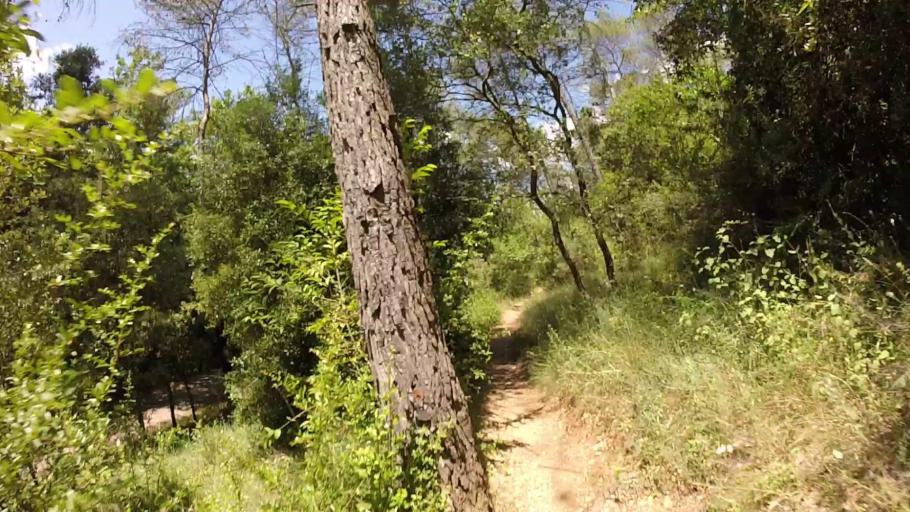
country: FR
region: Provence-Alpes-Cote d'Azur
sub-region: Departement des Alpes-Maritimes
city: Mougins
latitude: 43.6022
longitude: 7.0285
